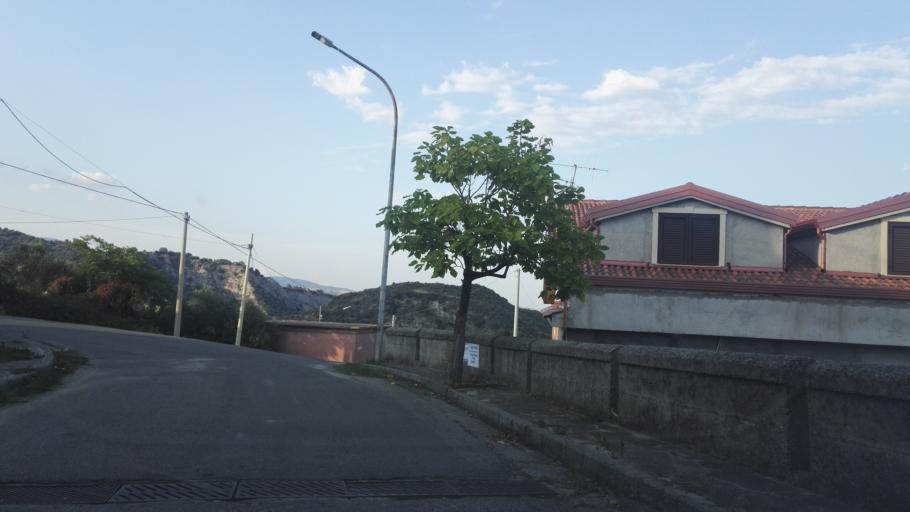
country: IT
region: Calabria
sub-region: Provincia di Reggio Calabria
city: Camini
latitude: 38.4330
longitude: 16.4841
